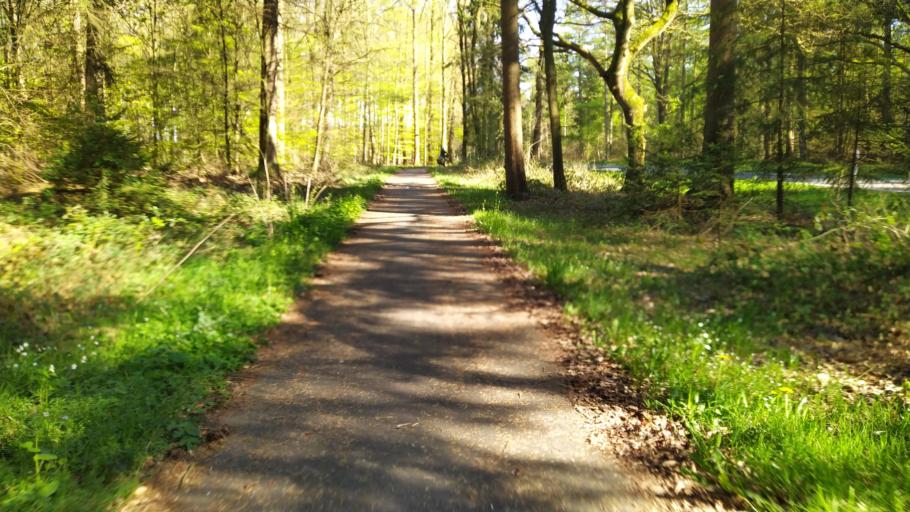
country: DE
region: Lower Saxony
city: Klein Meckelsen
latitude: 53.2948
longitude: 9.4219
